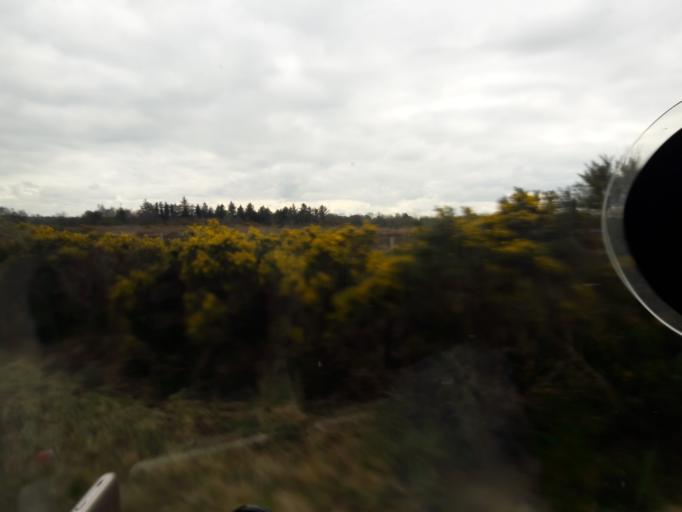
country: IE
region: Leinster
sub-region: An Longfort
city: Edgeworthstown
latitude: 53.6781
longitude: -7.5453
